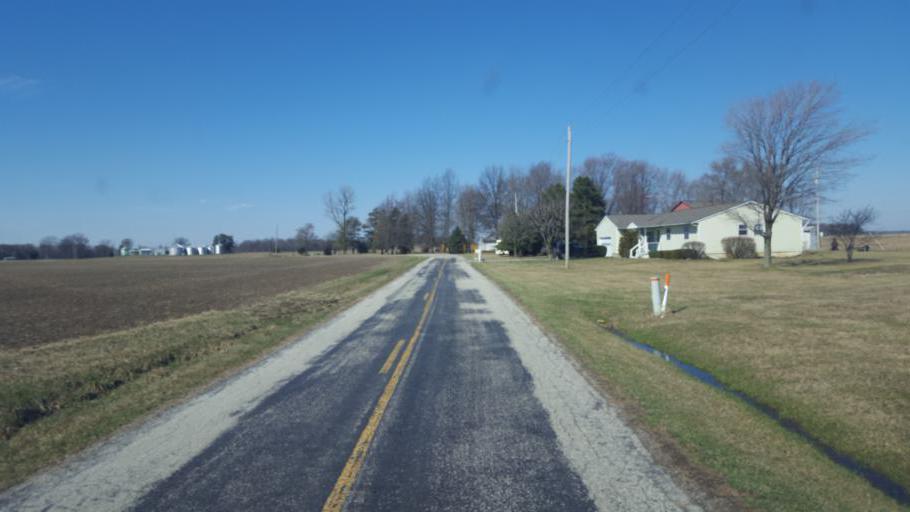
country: US
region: Ohio
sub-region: Morrow County
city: Cardington
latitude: 40.4913
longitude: -82.9772
